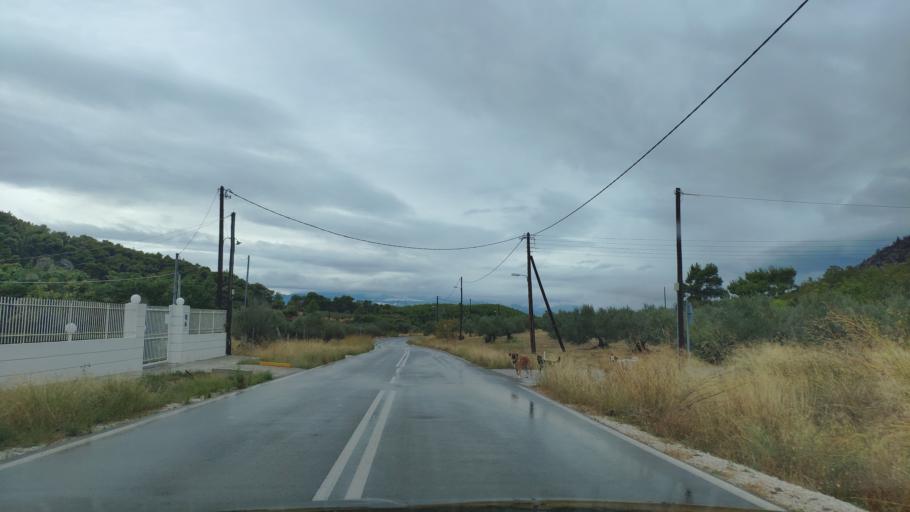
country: GR
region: Peloponnese
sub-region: Nomos Korinthias
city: Perachora
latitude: 38.0287
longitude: 22.9376
